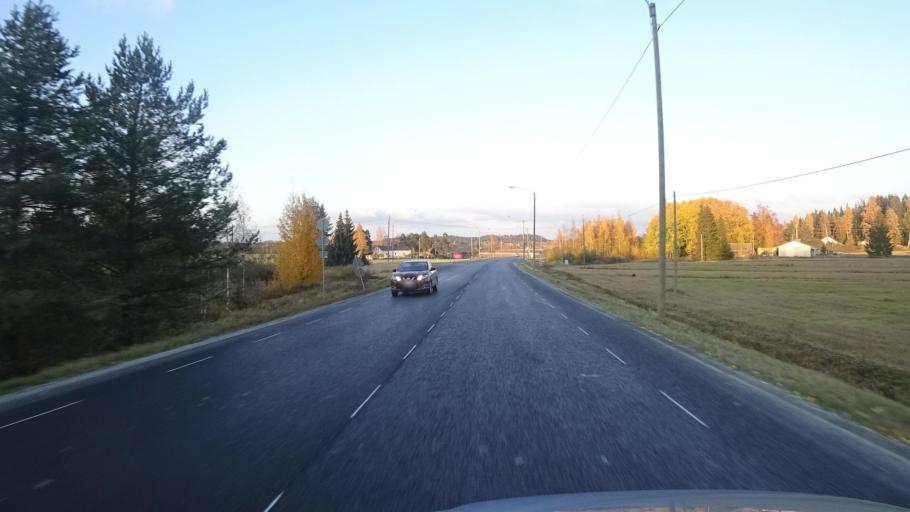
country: FI
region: Haeme
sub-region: Forssa
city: Jokioinen
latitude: 60.8192
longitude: 23.5487
